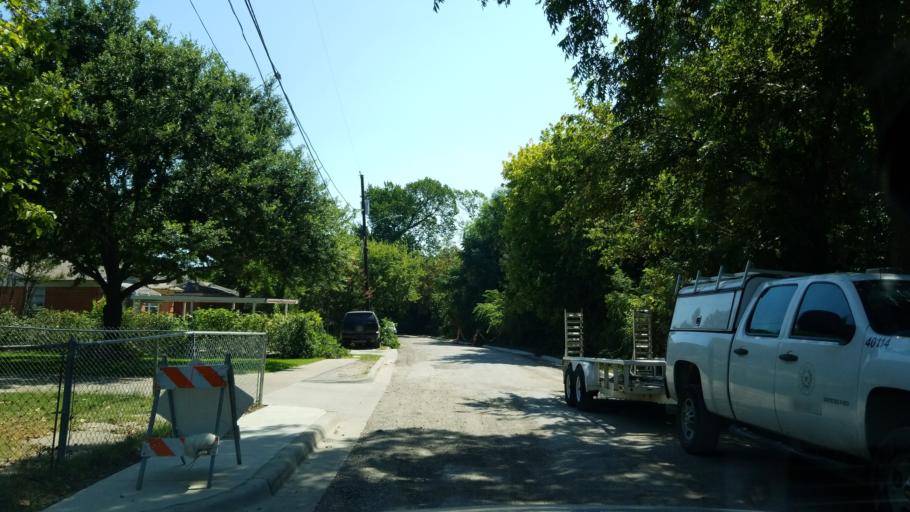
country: US
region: Texas
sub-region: Dallas County
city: Cockrell Hill
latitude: 32.7397
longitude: -96.8841
